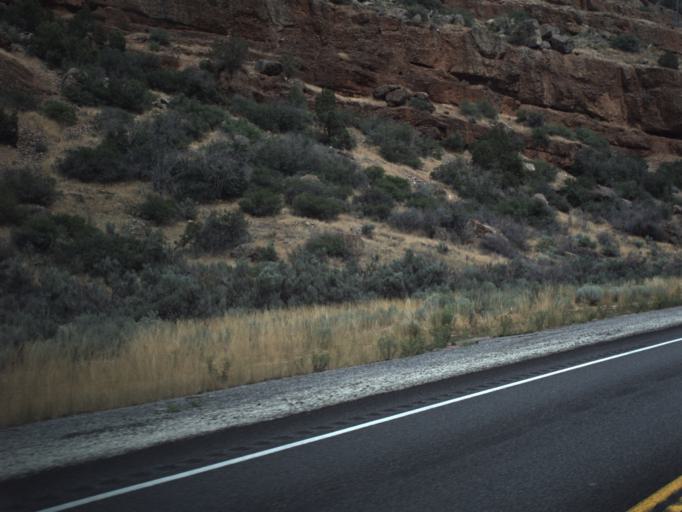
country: US
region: Utah
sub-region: Utah County
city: Mapleton
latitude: 39.9911
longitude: -111.3793
